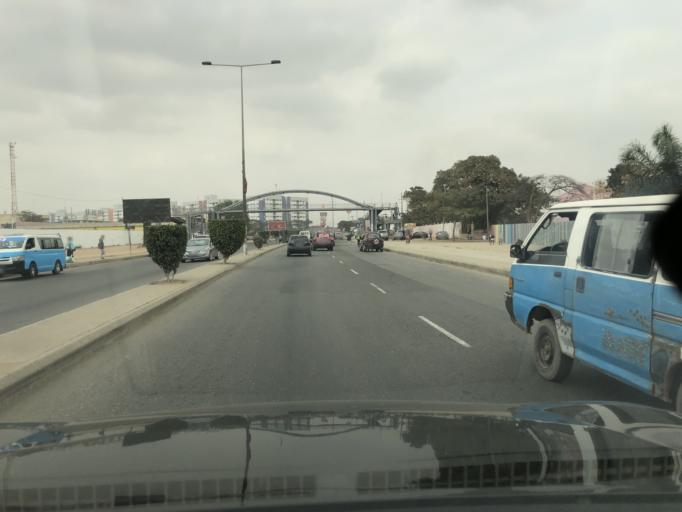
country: AO
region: Luanda
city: Luanda
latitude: -8.8442
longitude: 13.2843
